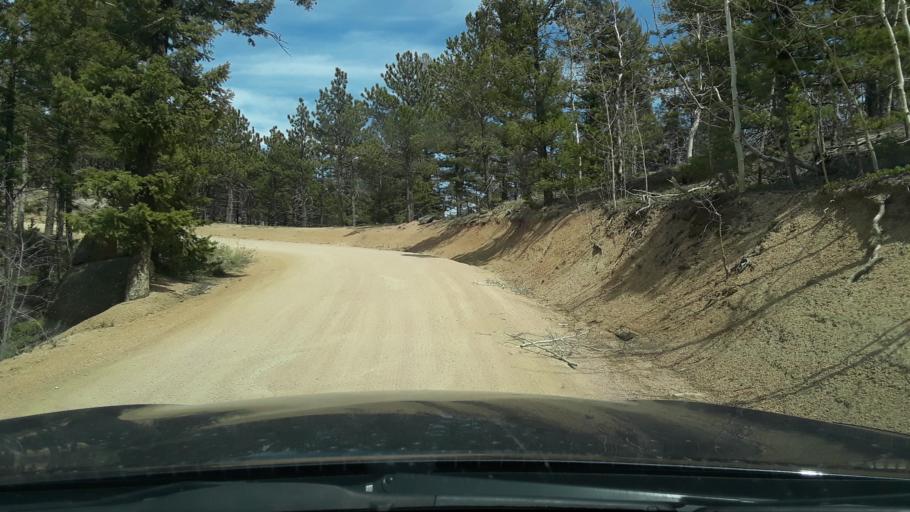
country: US
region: Colorado
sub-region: El Paso County
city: Palmer Lake
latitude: 39.0685
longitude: -104.9607
